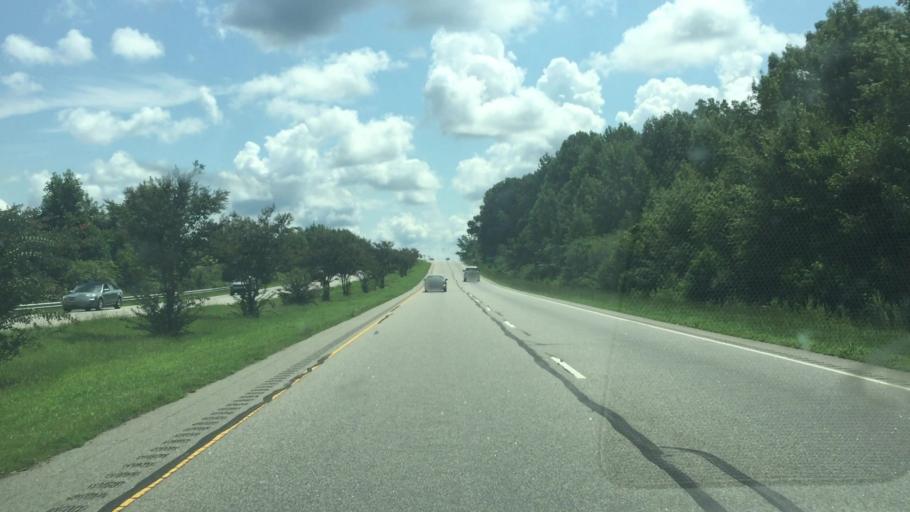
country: US
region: North Carolina
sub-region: Anson County
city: Wadesboro
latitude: 34.9626
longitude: -79.9957
